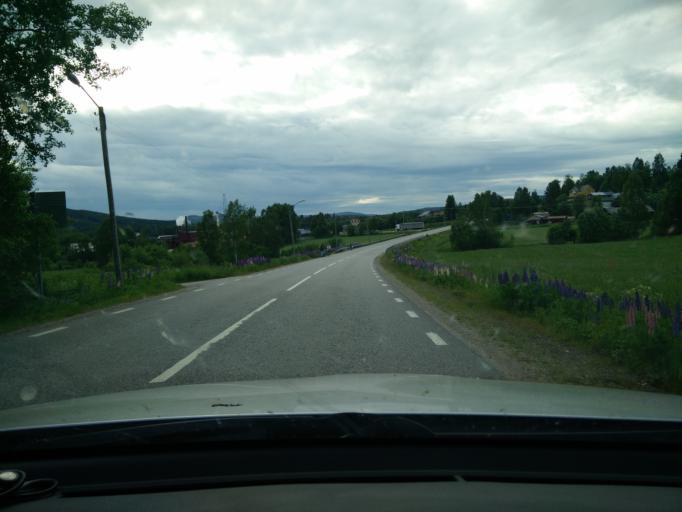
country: SE
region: Gaevleborg
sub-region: Hudiksvalls Kommun
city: Delsbo
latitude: 62.0999
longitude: 16.7303
